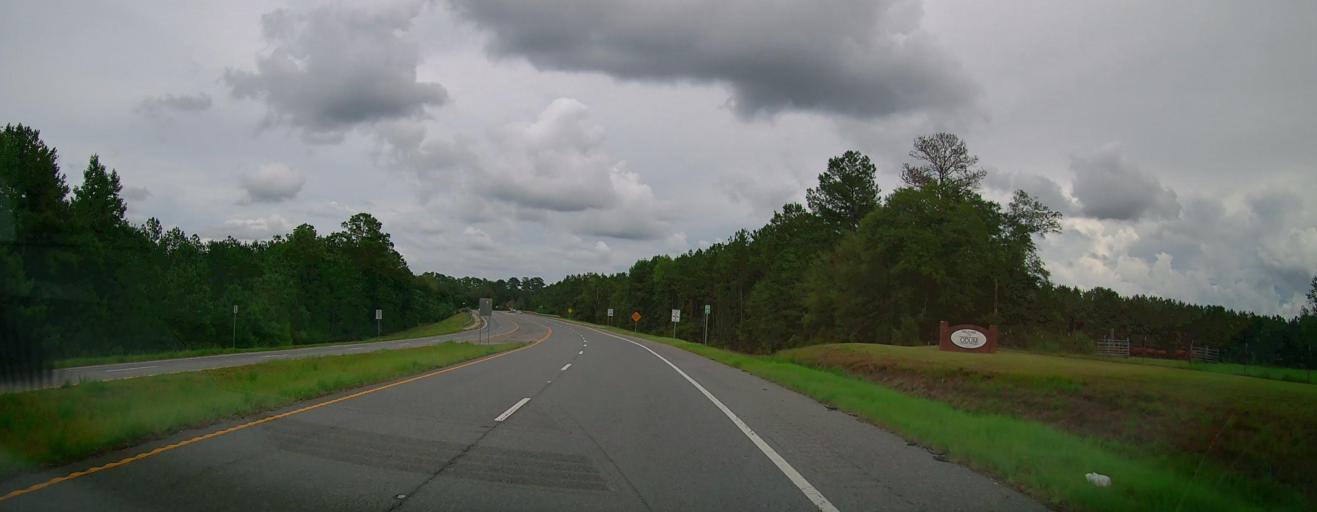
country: US
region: Georgia
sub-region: Wayne County
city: Jesup
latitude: 31.6678
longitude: -82.0443
